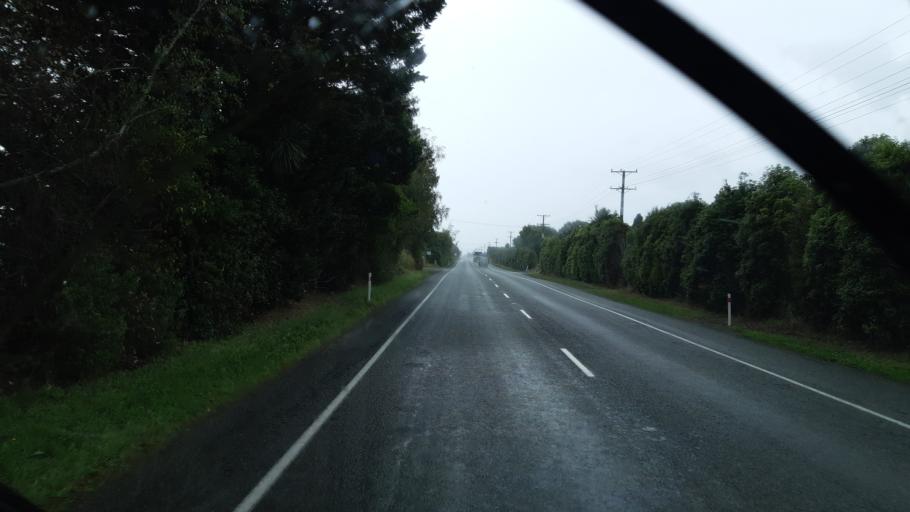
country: NZ
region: Tasman
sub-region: Tasman District
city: Brightwater
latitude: -41.3673
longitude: 173.1328
